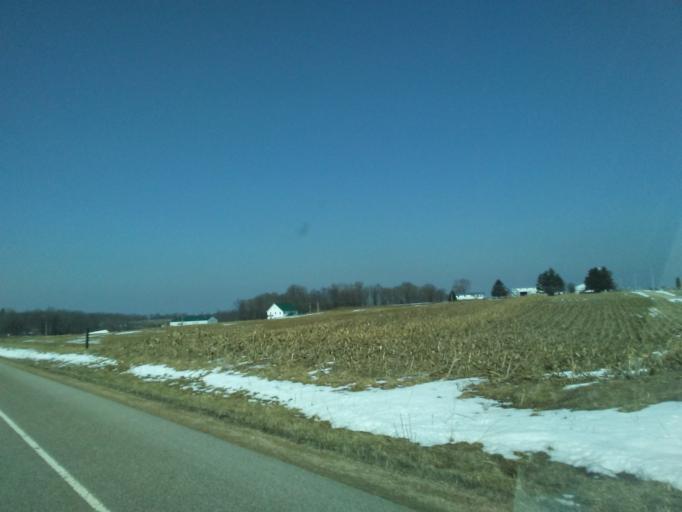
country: US
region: Wisconsin
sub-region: Richland County
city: Richland Center
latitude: 43.4169
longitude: -90.6426
